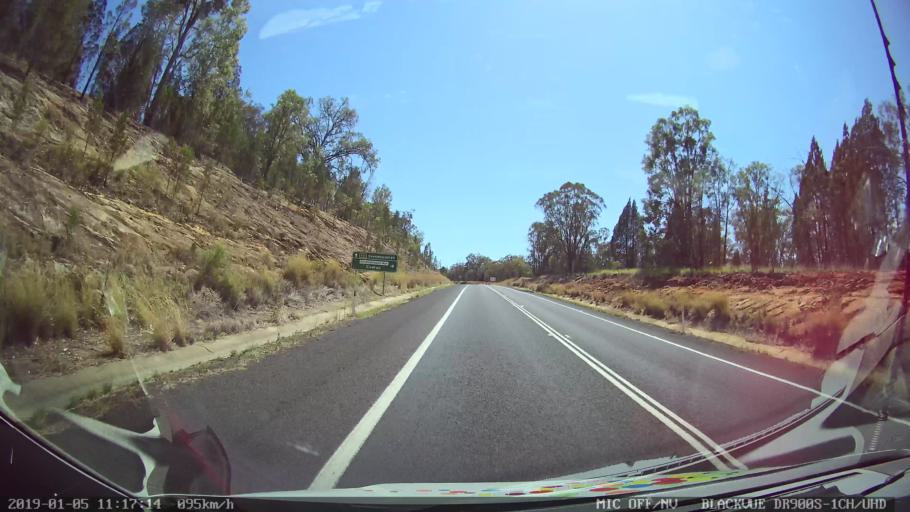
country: AU
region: New South Wales
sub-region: Warrumbungle Shire
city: Coonabarabran
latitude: -31.3288
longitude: 149.3049
